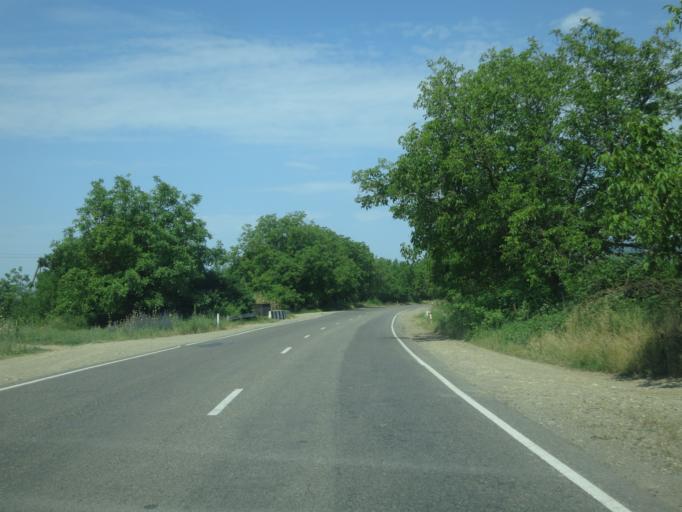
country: GE
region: Kakheti
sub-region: Gurjaani
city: Gurjaani
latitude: 41.6311
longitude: 45.6979
